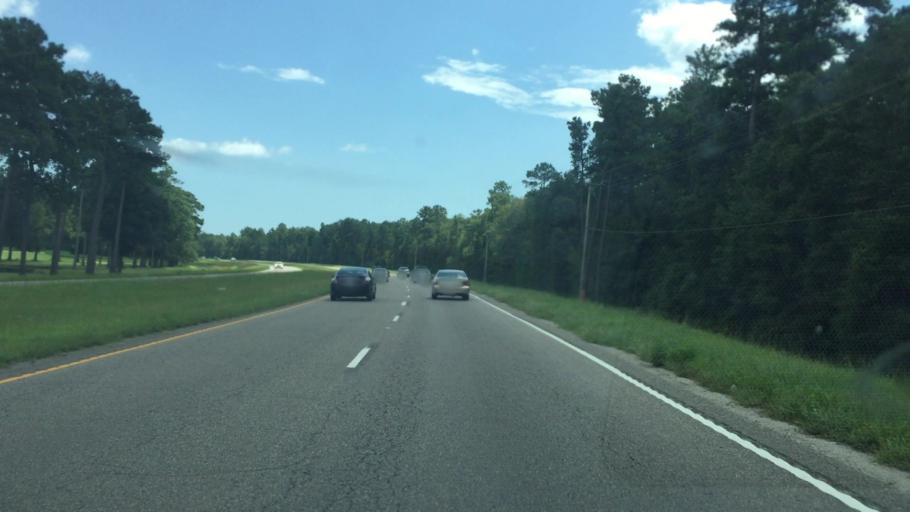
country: US
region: South Carolina
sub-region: Horry County
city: North Myrtle Beach
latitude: 33.9200
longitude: -78.7245
